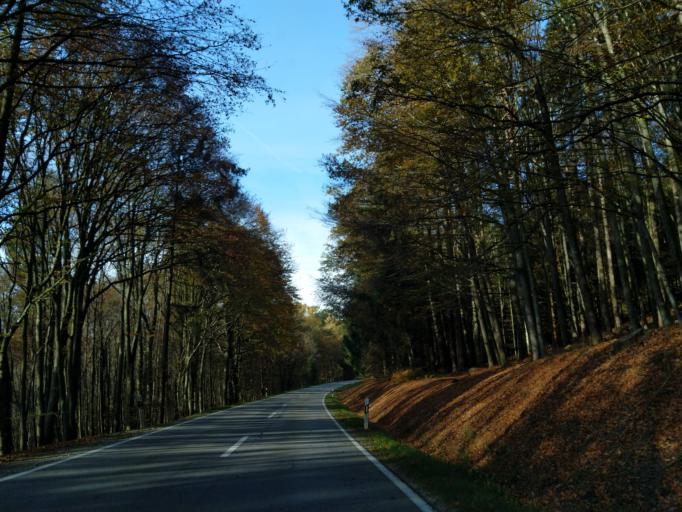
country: DE
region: Bavaria
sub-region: Lower Bavaria
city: Grattersdorf
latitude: 48.8018
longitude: 13.1713
